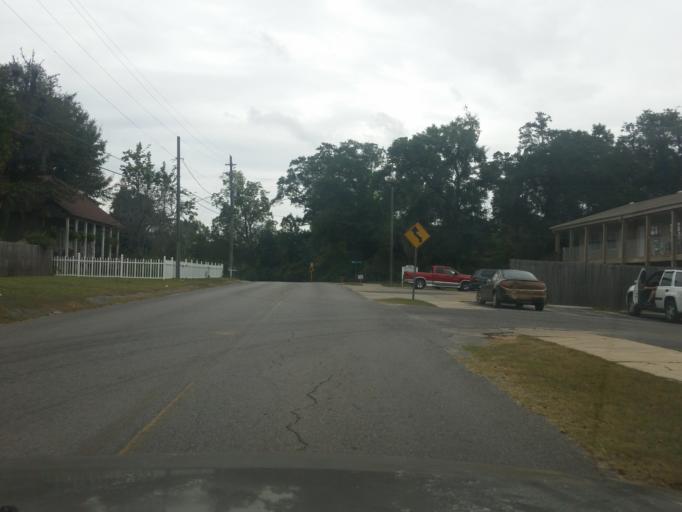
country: US
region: Florida
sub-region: Santa Rosa County
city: Milton
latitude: 30.6300
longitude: -87.0375
